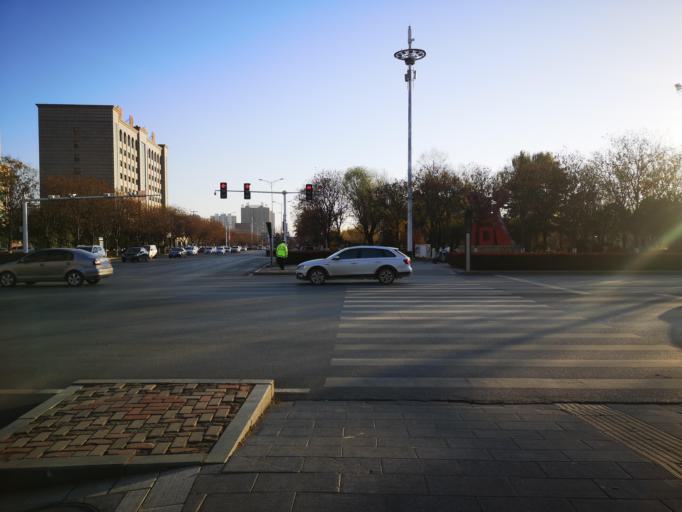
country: CN
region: Henan Sheng
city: Puyang
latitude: 35.7731
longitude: 115.0049
